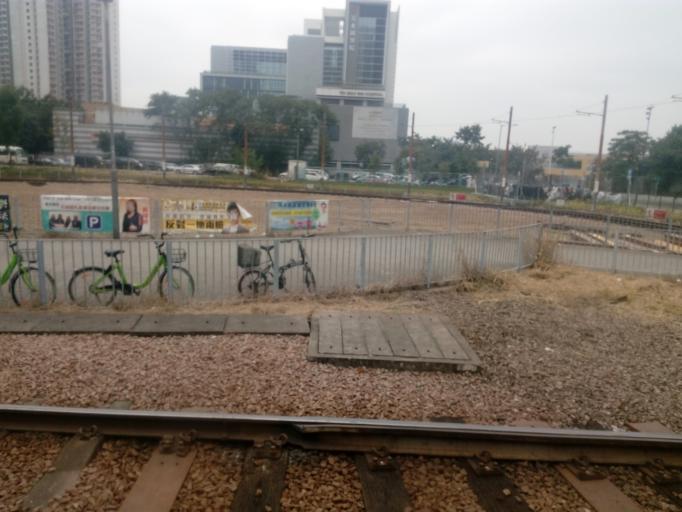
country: HK
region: Yuen Long
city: Yuen Long Kau Hui
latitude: 22.4595
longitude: 113.9974
